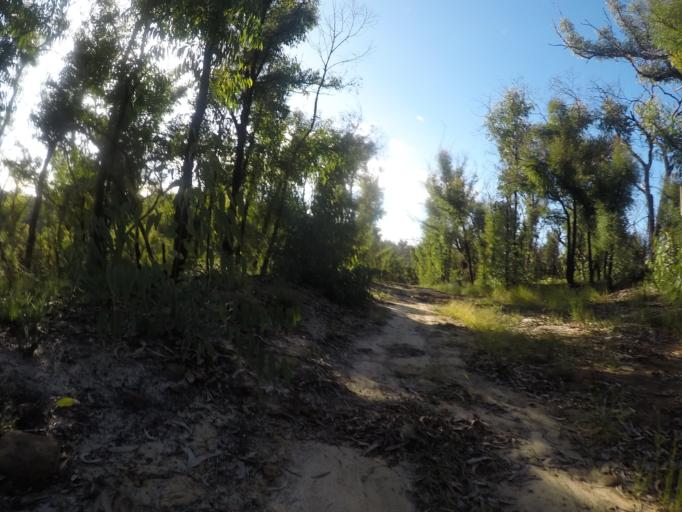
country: AU
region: New South Wales
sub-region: Hornsby Shire
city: Glenorie
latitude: -33.3495
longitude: 151.0074
